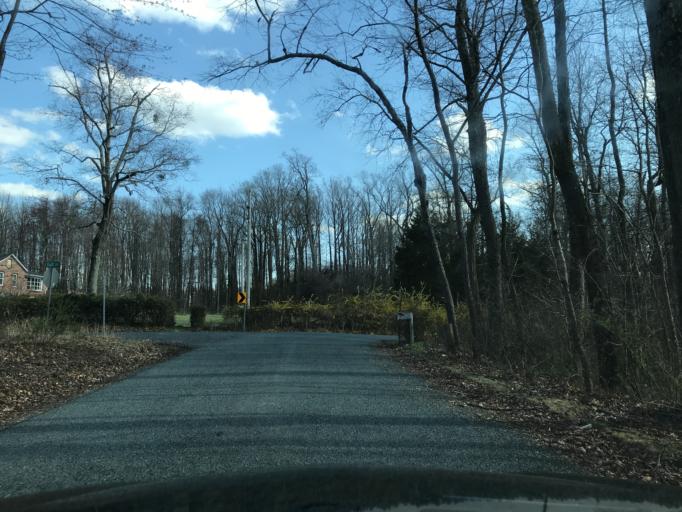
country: US
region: Maryland
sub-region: Harford County
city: Riverside
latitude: 39.4460
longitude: -76.2299
